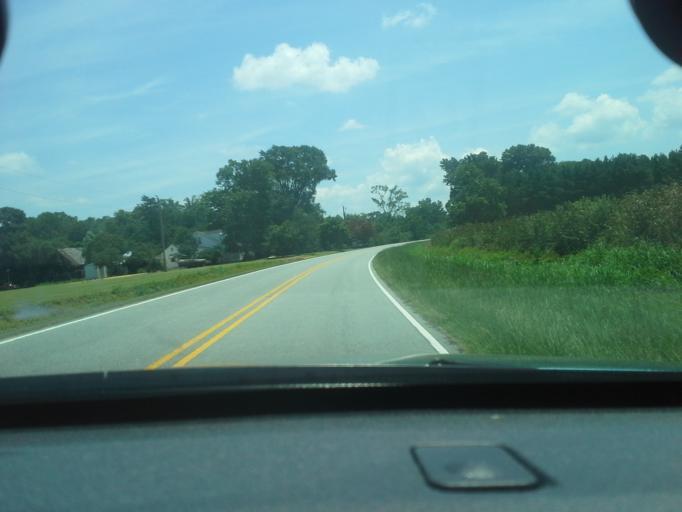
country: US
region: North Carolina
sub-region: Chowan County
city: Edenton
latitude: 35.9293
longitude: -76.6055
